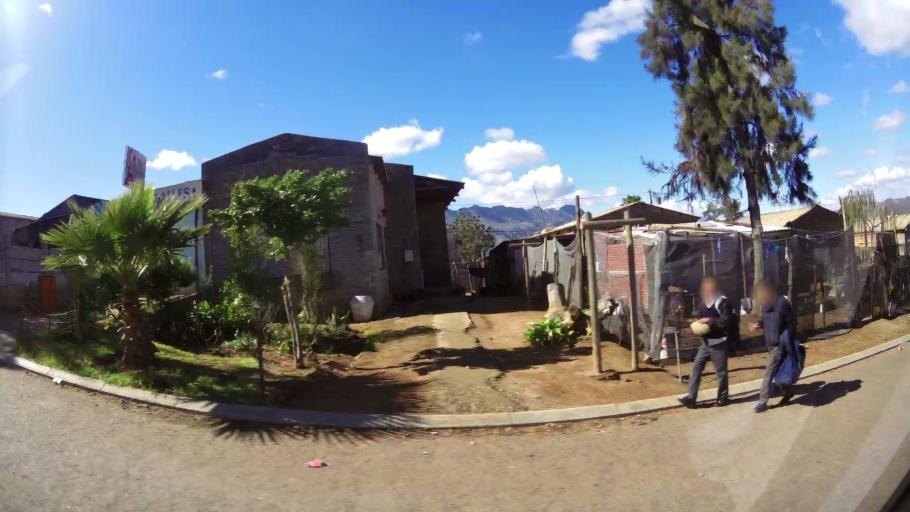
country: ZA
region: Western Cape
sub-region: Cape Winelands District Municipality
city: Ashton
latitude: -33.8310
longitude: 20.0420
